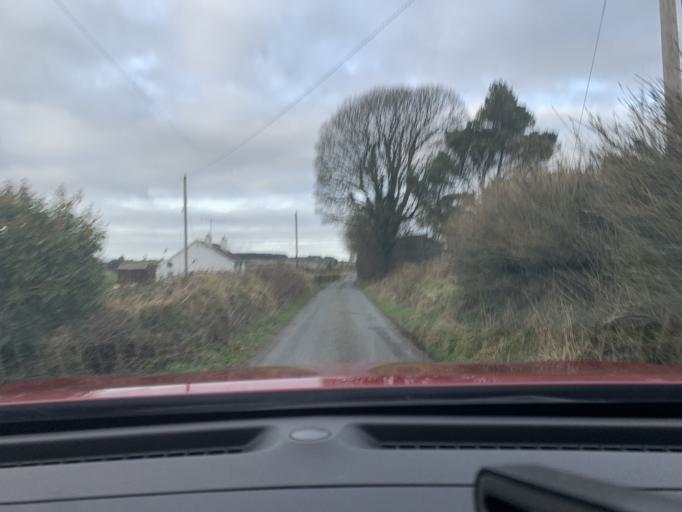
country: IE
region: Connaught
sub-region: Roscommon
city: Ballaghaderreen
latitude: 53.9670
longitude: -8.5595
